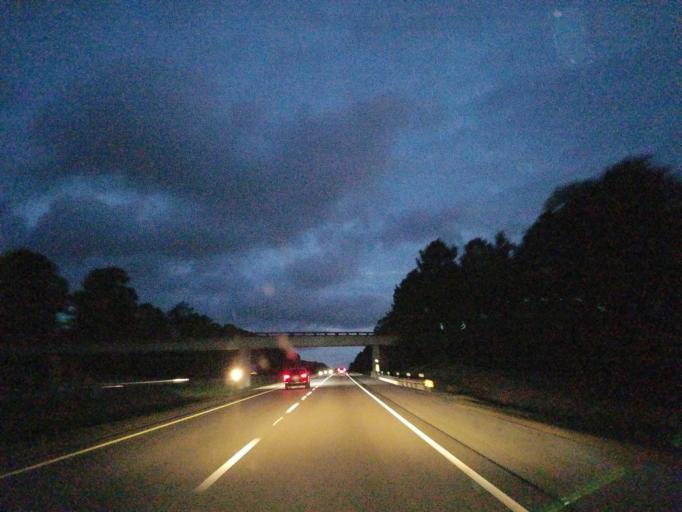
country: US
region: Mississippi
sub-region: Jones County
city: Sharon
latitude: 31.8383
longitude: -89.0499
